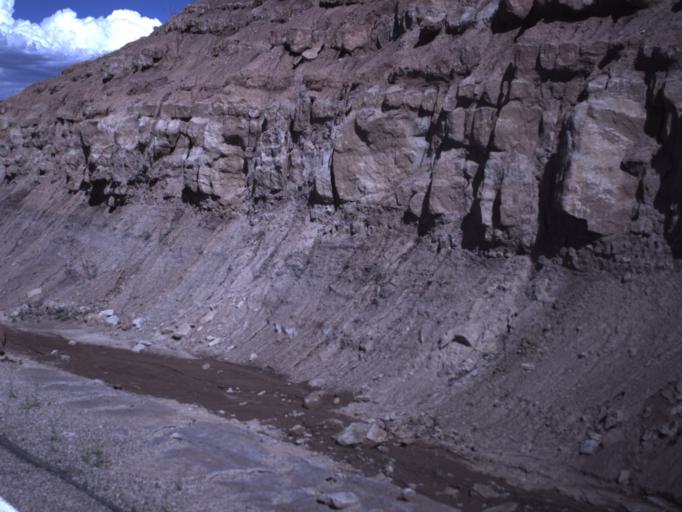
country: US
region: Utah
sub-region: Duchesne County
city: Duchesne
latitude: 40.3176
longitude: -110.6969
